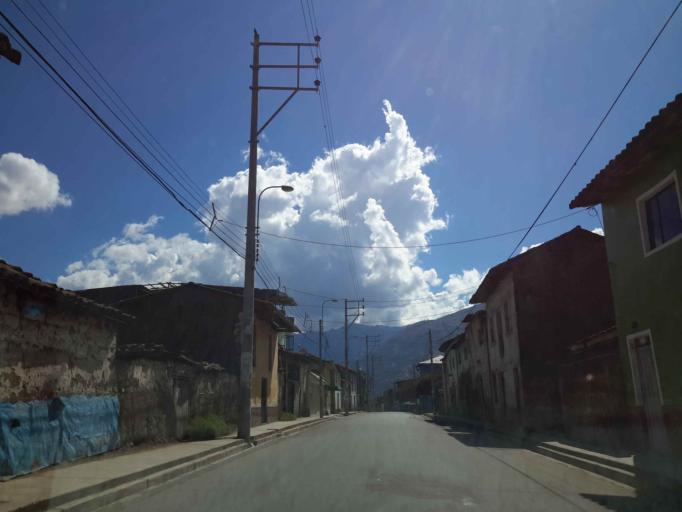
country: PE
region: Apurimac
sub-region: Provincia de Andahuaylas
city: Talavera
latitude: -13.6549
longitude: -73.4241
